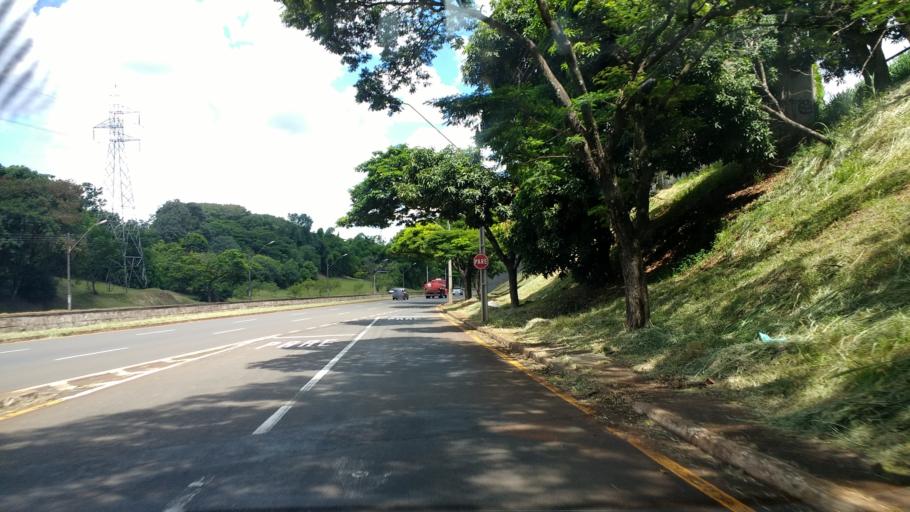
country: BR
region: Parana
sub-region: Londrina
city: Londrina
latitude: -23.3221
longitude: -51.1485
